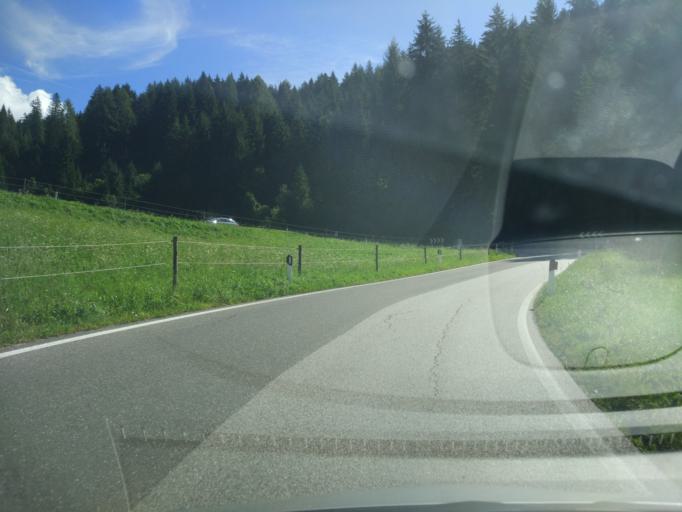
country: IT
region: Trentino-Alto Adige
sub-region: Provincia di Trento
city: Predazzo
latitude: 46.3146
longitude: 11.6488
